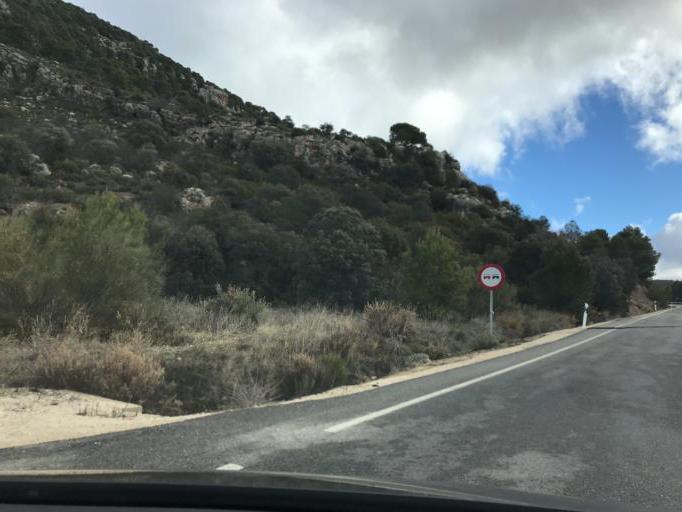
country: ES
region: Andalusia
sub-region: Provincia de Jaen
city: Huelma
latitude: 37.6907
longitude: -3.5039
